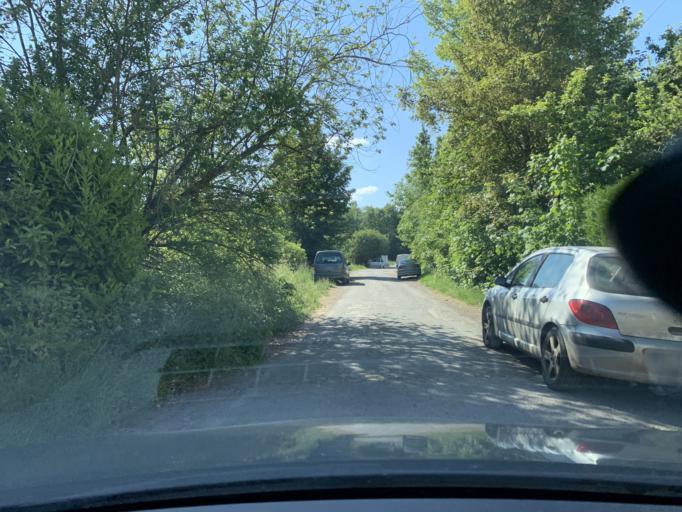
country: FR
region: Nord-Pas-de-Calais
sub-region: Departement du Pas-de-Calais
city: Oisy-le-Verger
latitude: 50.2640
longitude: 3.1383
